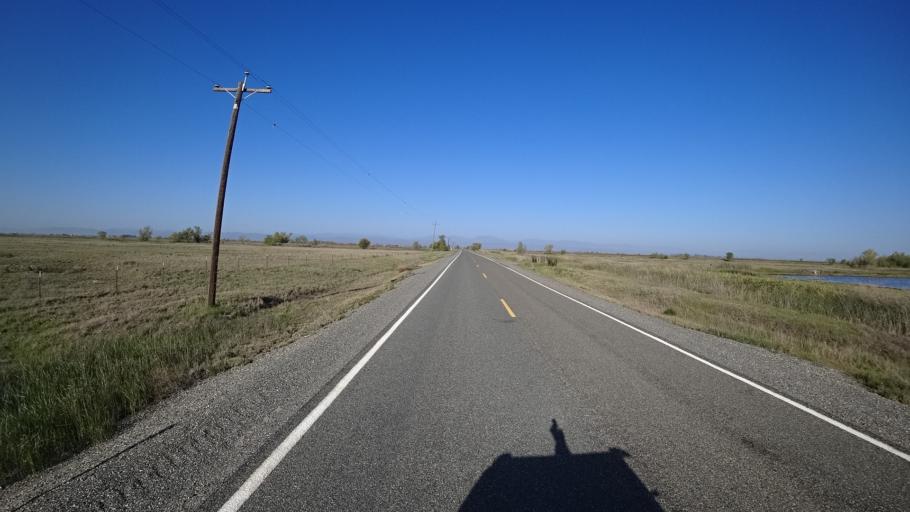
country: US
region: California
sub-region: Glenn County
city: Willows
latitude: 39.4074
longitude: -122.1410
